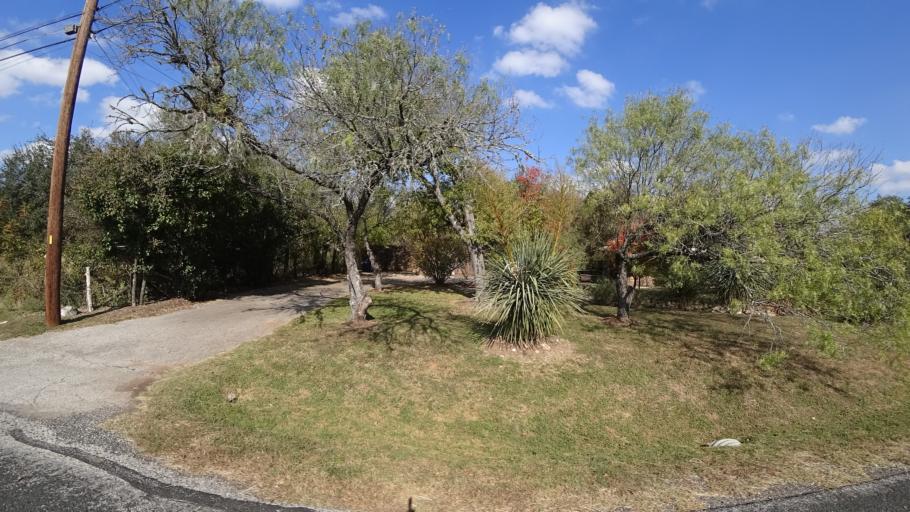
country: US
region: Texas
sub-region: Travis County
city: Shady Hollow
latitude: 30.1815
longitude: -97.8487
